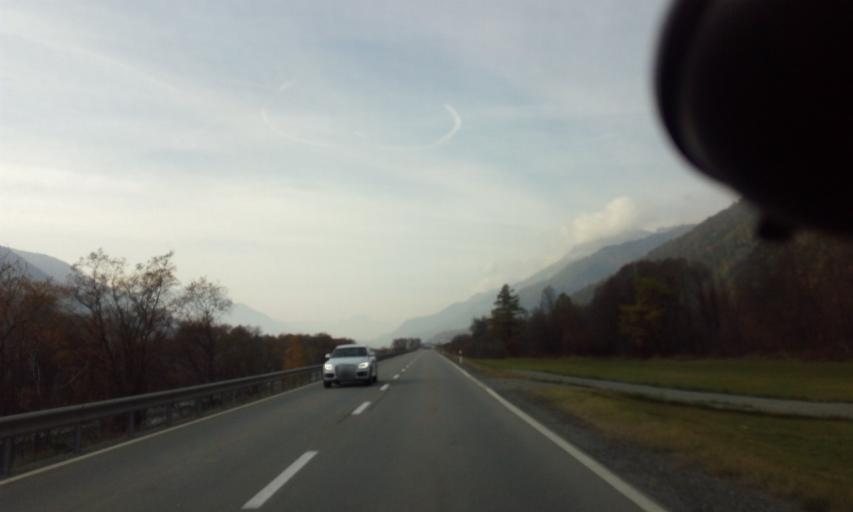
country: CH
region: Grisons
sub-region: Maloja District
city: Ponte
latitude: 46.5687
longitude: 9.9134
